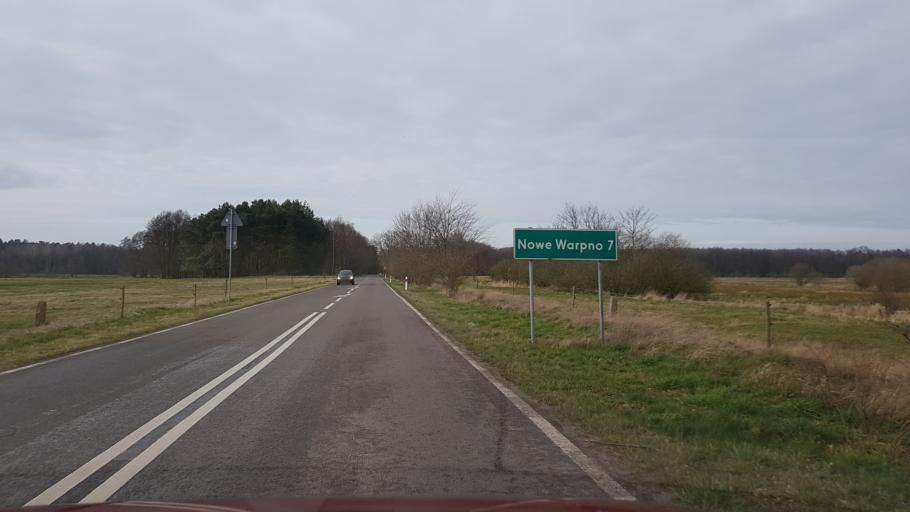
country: PL
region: West Pomeranian Voivodeship
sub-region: Powiat policki
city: Nowe Warpno
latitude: 53.6967
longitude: 14.3494
